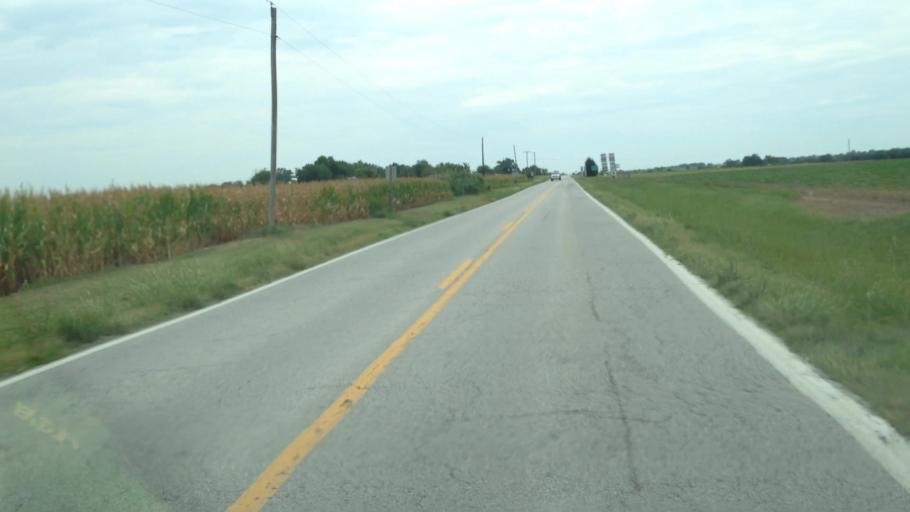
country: US
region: Oklahoma
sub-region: Delaware County
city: Cleora
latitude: 36.6238
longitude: -94.9815
